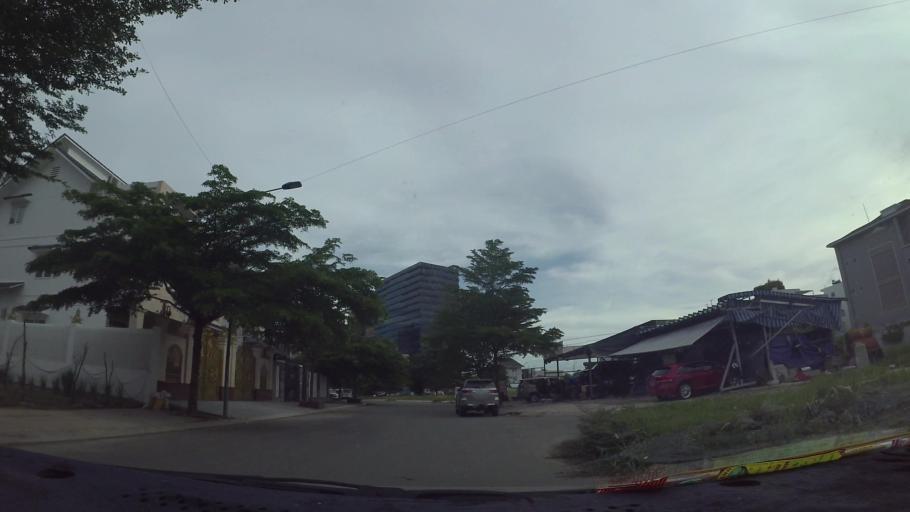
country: VN
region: Ho Chi Minh City
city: Quan Sau
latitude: 10.7458
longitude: 106.6555
